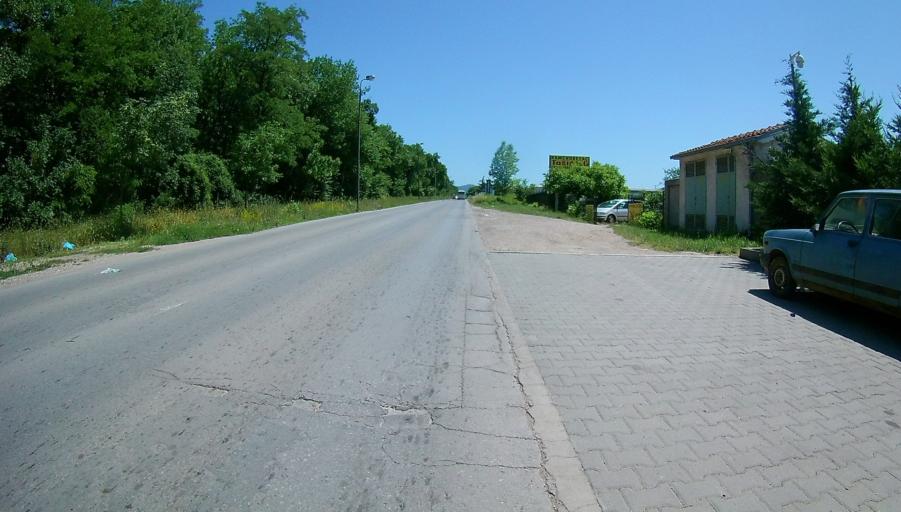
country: RS
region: Central Serbia
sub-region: Nisavski Okrug
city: Nis
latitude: 43.3023
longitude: 21.8718
